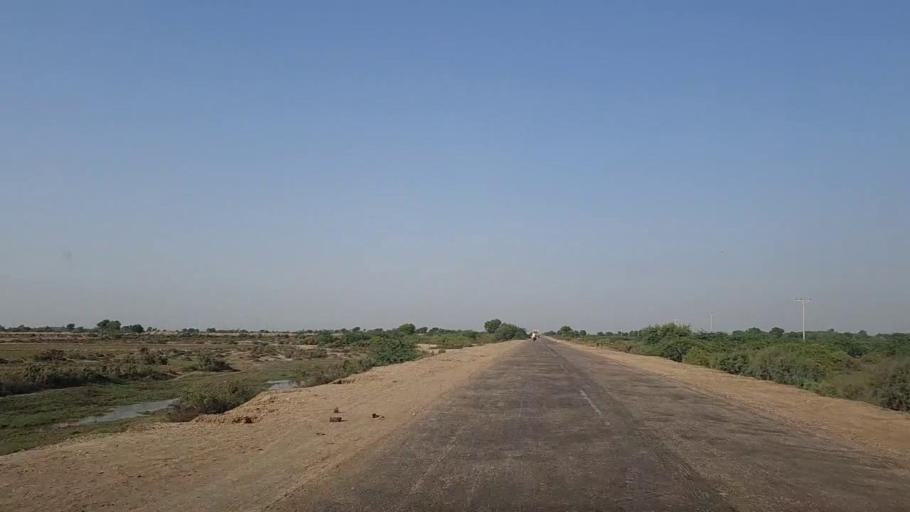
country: PK
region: Sindh
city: Mirpur Batoro
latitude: 24.6196
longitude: 68.4060
